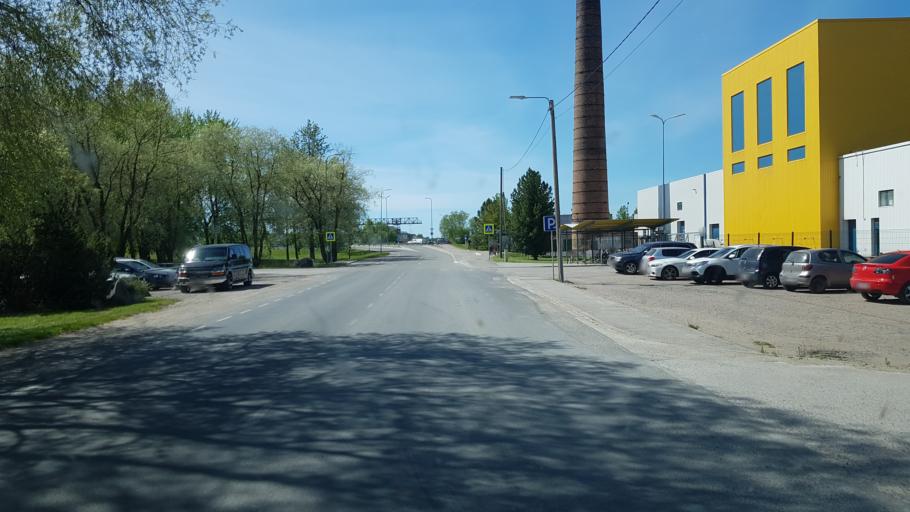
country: EE
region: Saare
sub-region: Kuressaare linn
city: Kuressaare
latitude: 58.2698
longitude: 22.4917
